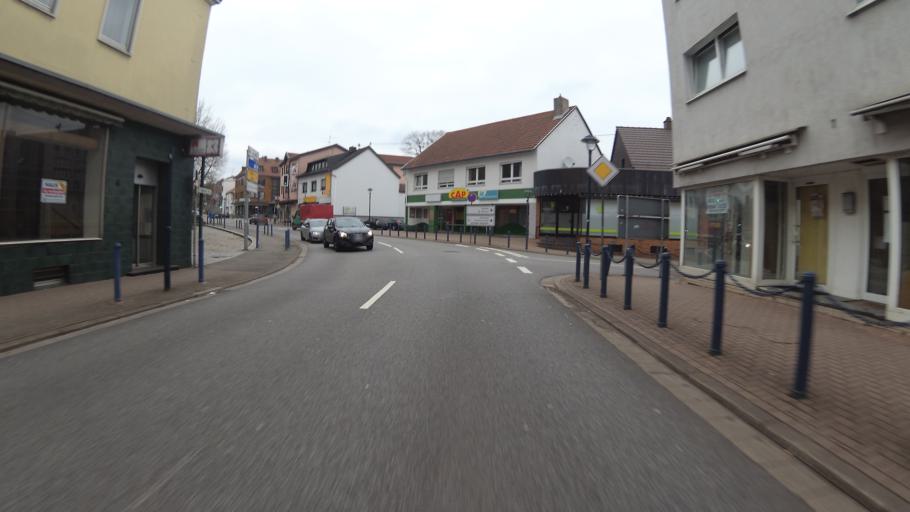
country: DE
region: Saarland
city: Spiesen-Elversberg
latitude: 49.3137
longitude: 7.1275
